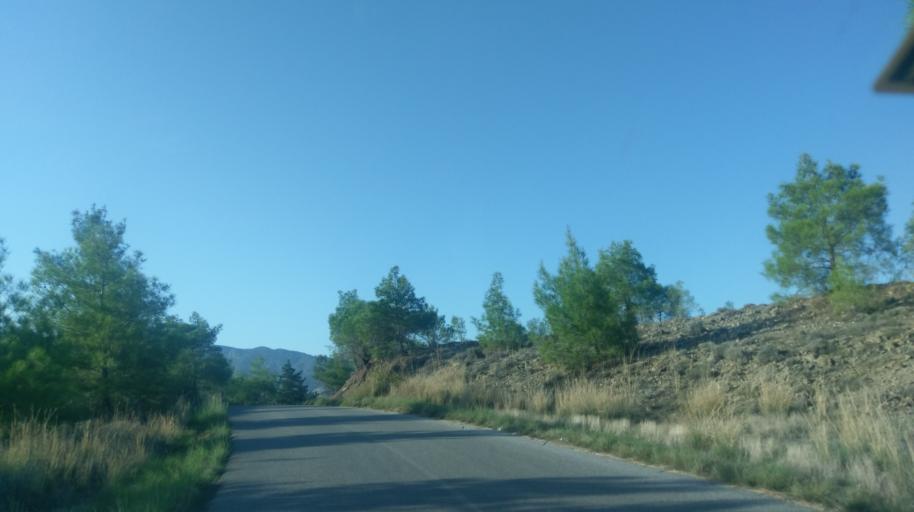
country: CY
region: Ammochostos
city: Lefkonoiko
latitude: 35.2901
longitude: 33.6518
